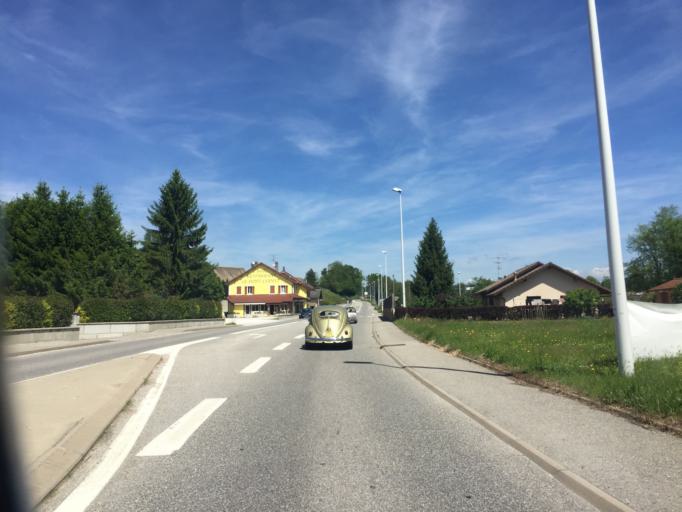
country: FR
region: Rhone-Alpes
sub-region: Departement de la Haute-Savoie
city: Vallieres
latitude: 45.8897
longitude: 5.9379
